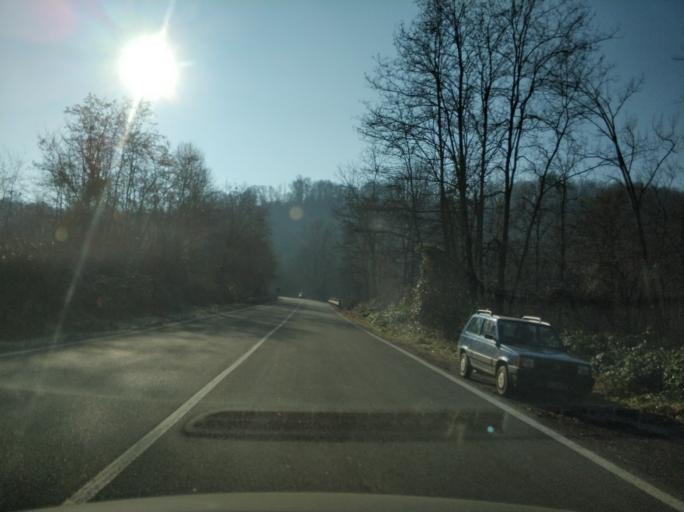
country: IT
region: Piedmont
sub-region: Provincia di Torino
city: Rocca Canavese
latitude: 45.2881
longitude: 7.5831
